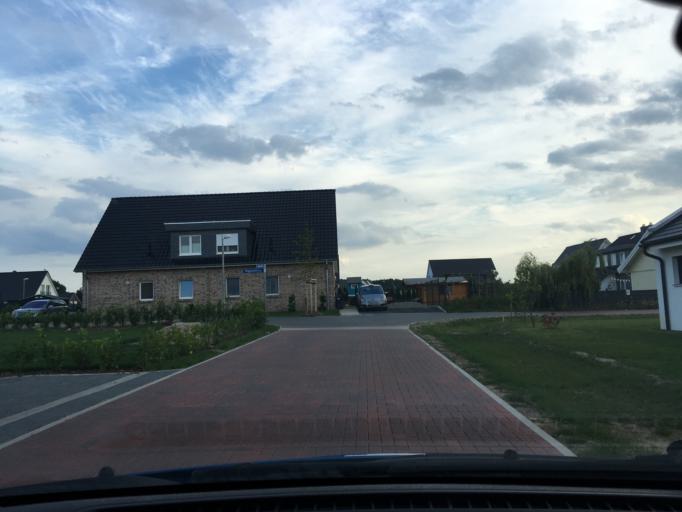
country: DE
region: Lower Saxony
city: Westergellersen
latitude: 53.2347
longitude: 10.2531
